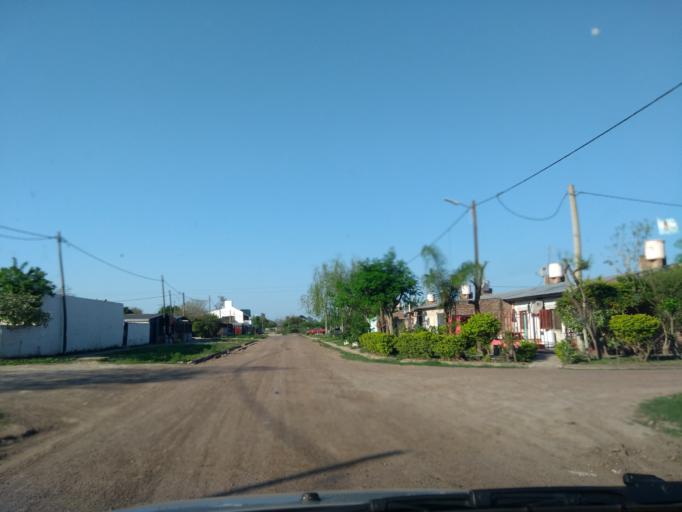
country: AR
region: Chaco
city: Fontana
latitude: -27.4133
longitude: -59.0563
